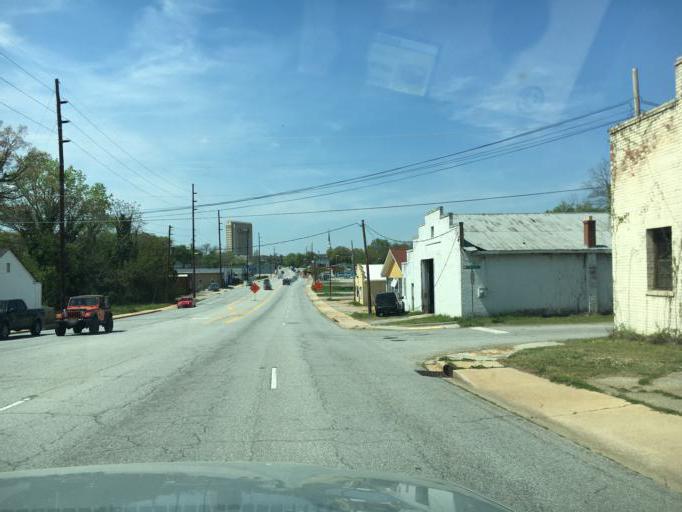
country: US
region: South Carolina
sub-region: Spartanburg County
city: Spartanburg
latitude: 34.9452
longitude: -81.9187
